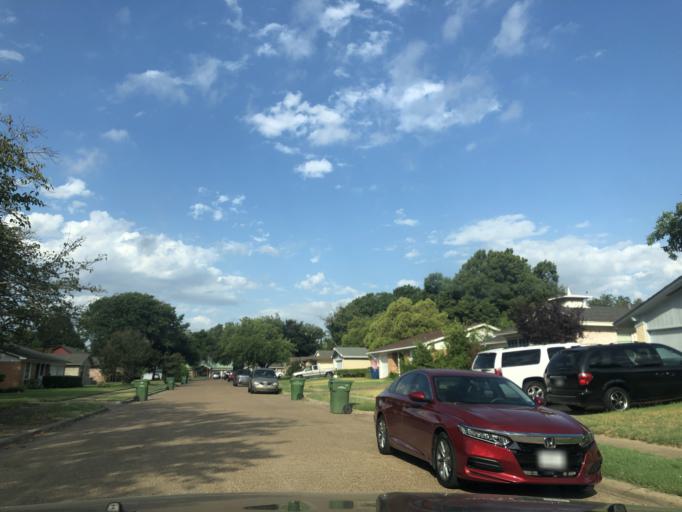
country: US
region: Texas
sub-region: Dallas County
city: Garland
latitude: 32.8858
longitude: -96.6583
